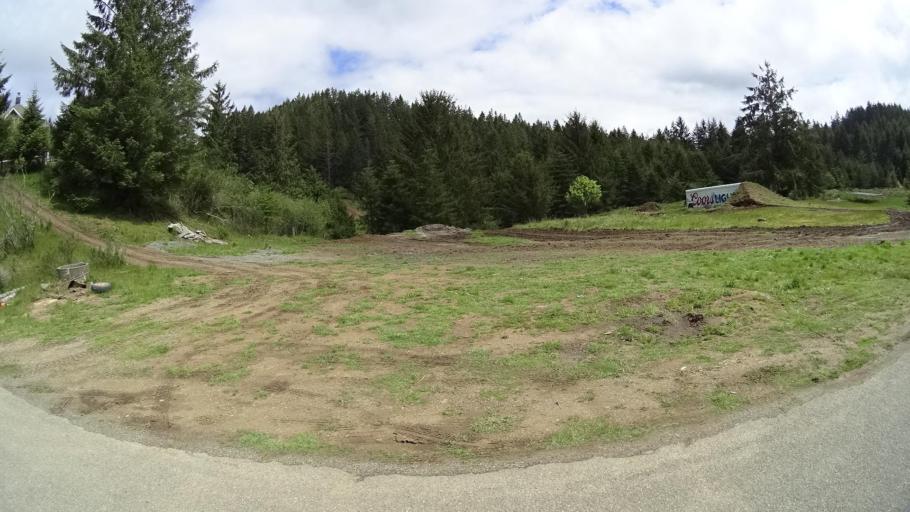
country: US
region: California
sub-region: Humboldt County
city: Bayside
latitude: 40.8360
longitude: -124.0225
